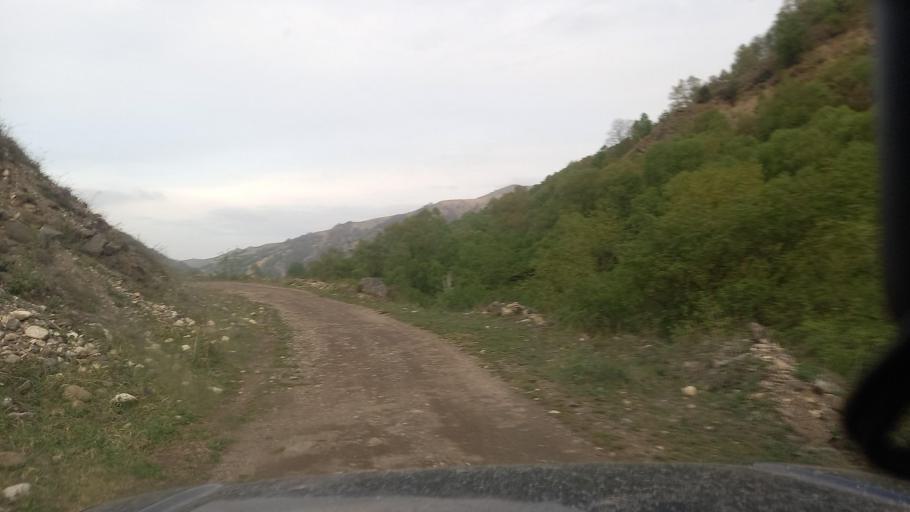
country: RU
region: Kabardino-Balkariya
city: Kamennomostskoye
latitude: 43.7209
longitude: 42.8625
